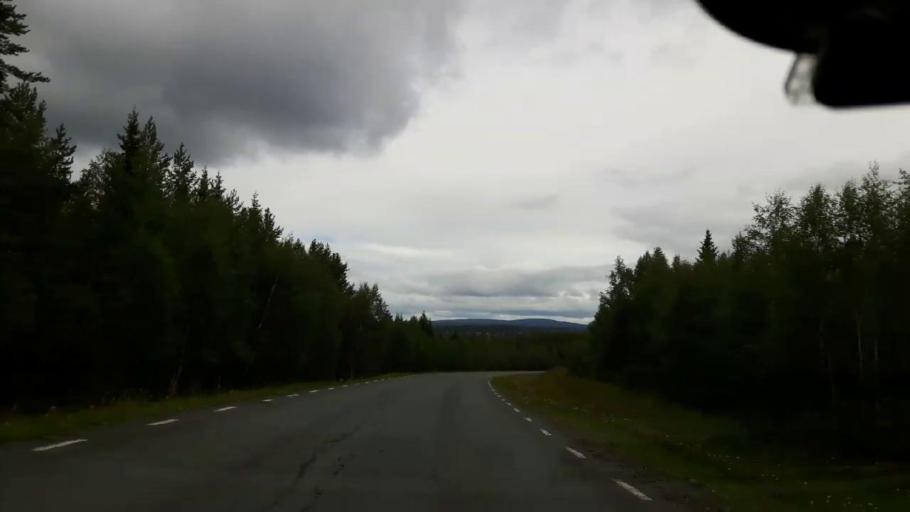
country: SE
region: Jaemtland
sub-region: Krokoms Kommun
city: Valla
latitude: 63.6218
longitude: 13.8112
